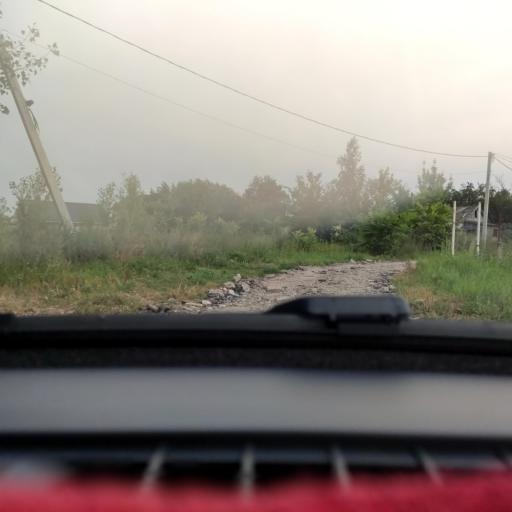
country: RU
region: Voronezj
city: Novaya Usman'
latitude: 51.6267
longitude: 39.3829
